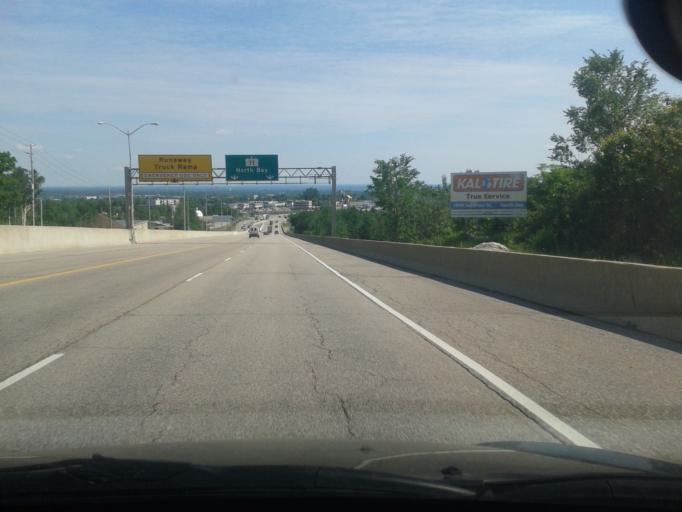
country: CA
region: Ontario
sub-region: Nipissing District
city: North Bay
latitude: 46.3408
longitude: -79.4695
